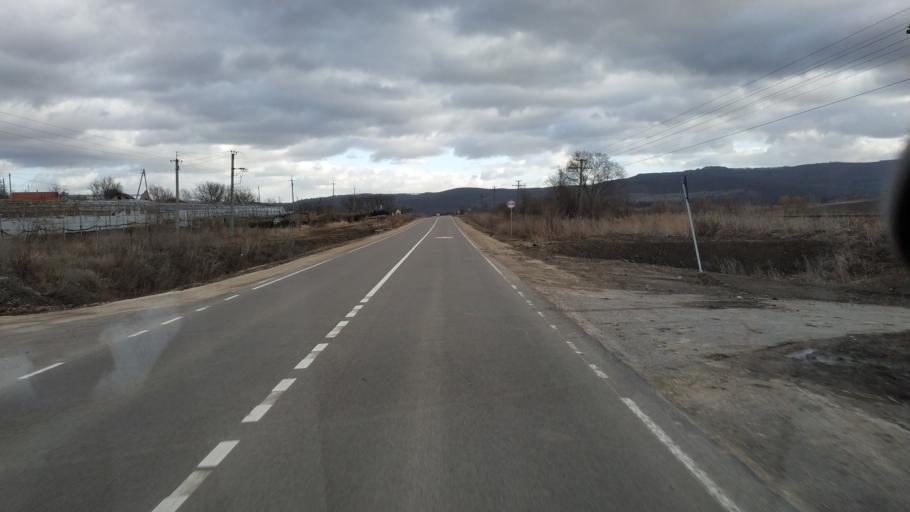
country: MD
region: Calarasi
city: Calarasi
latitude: 47.2617
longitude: 28.2364
